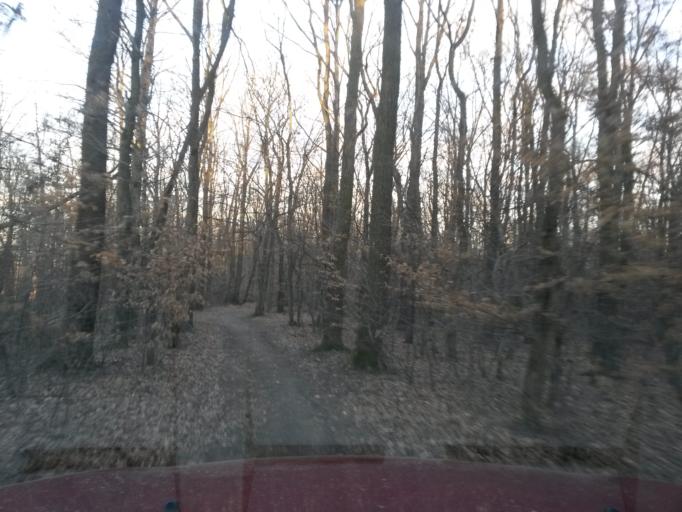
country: SK
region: Kosicky
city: Kosice
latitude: 48.7059
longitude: 21.2982
